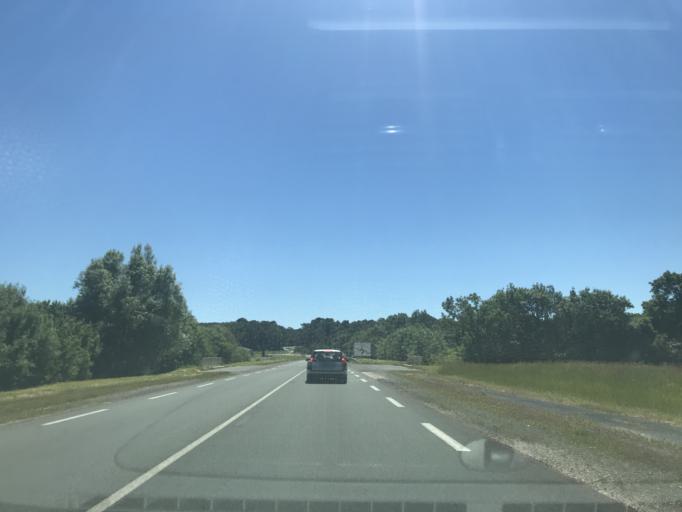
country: FR
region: Poitou-Charentes
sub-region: Departement de la Charente-Maritime
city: Saint-Georges-de-Didonne
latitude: 45.5997
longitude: -0.9739
